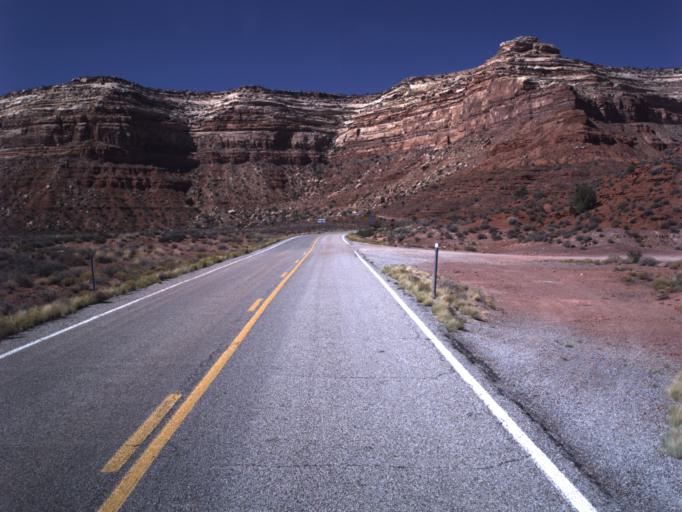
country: US
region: Utah
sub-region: San Juan County
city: Blanding
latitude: 37.2637
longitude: -109.9320
